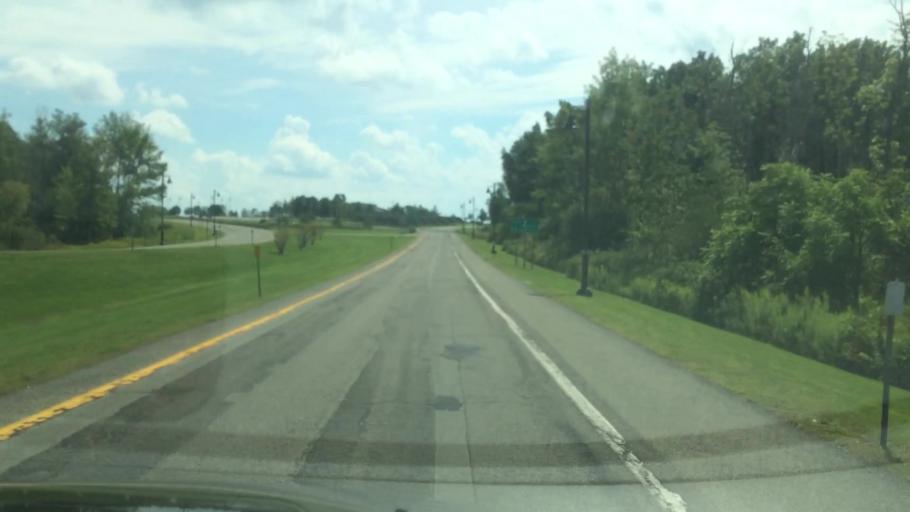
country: US
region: New York
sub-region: Chautauqua County
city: Lakewood
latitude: 42.1379
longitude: -79.3517
